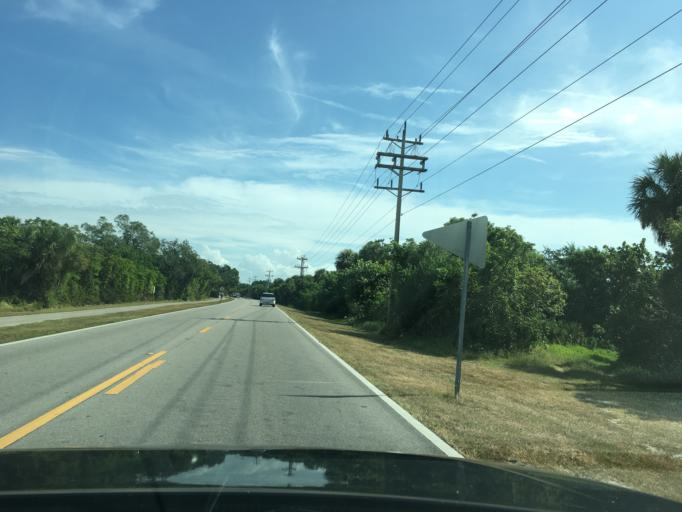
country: US
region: Florida
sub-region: Lee County
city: Saint James City
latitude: 26.4384
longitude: -82.0917
